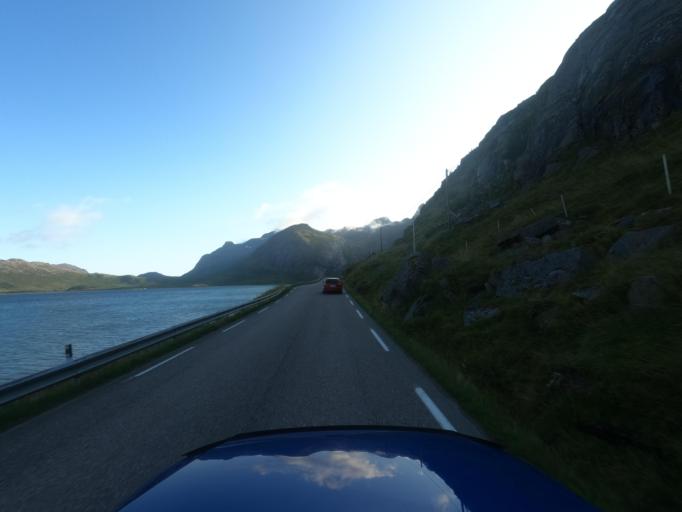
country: NO
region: Nordland
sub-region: Flakstad
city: Ramberg
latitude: 68.0959
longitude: 13.3181
